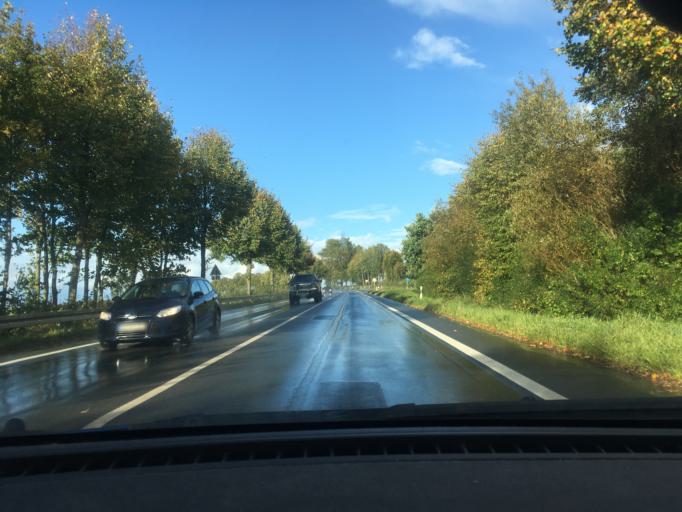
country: DE
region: Lower Saxony
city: Nordstemmen
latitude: 52.1694
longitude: 9.7436
